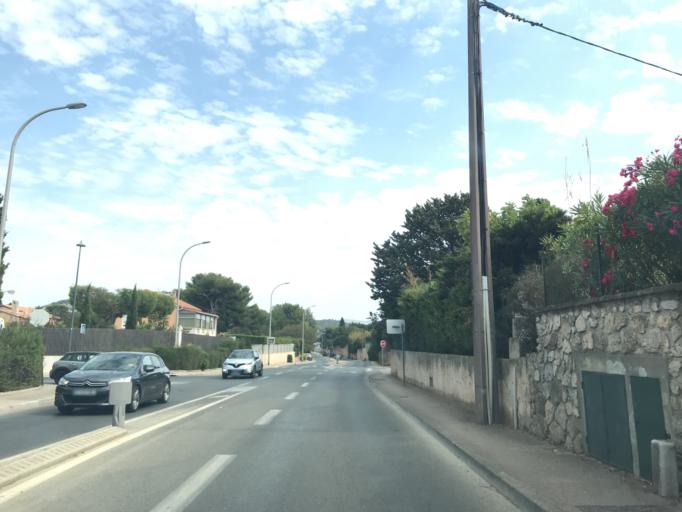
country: FR
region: Provence-Alpes-Cote d'Azur
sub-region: Departement du Var
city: Six-Fours-les-Plages
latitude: 43.0871
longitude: 5.8260
